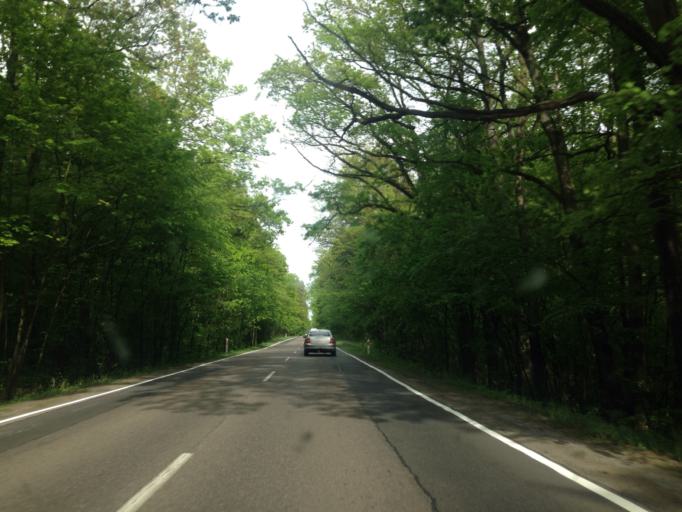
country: PL
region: Kujawsko-Pomorskie
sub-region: Powiat brodnicki
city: Brodnica
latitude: 53.2791
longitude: 19.4526
